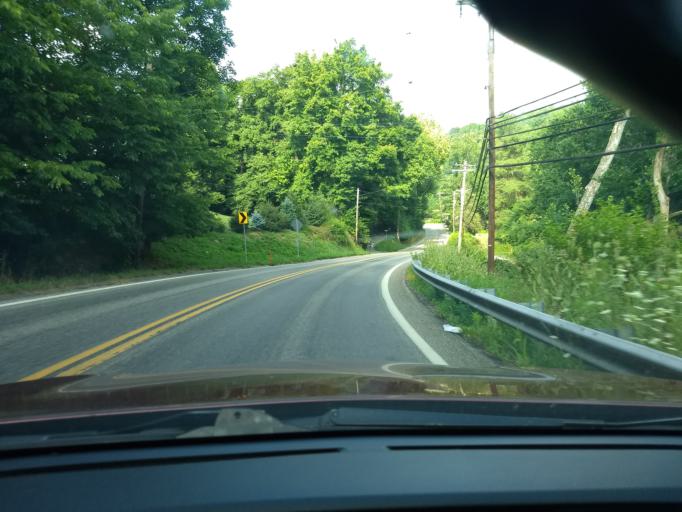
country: US
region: Pennsylvania
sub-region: Allegheny County
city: Bell Acres
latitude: 40.6010
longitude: -80.1888
